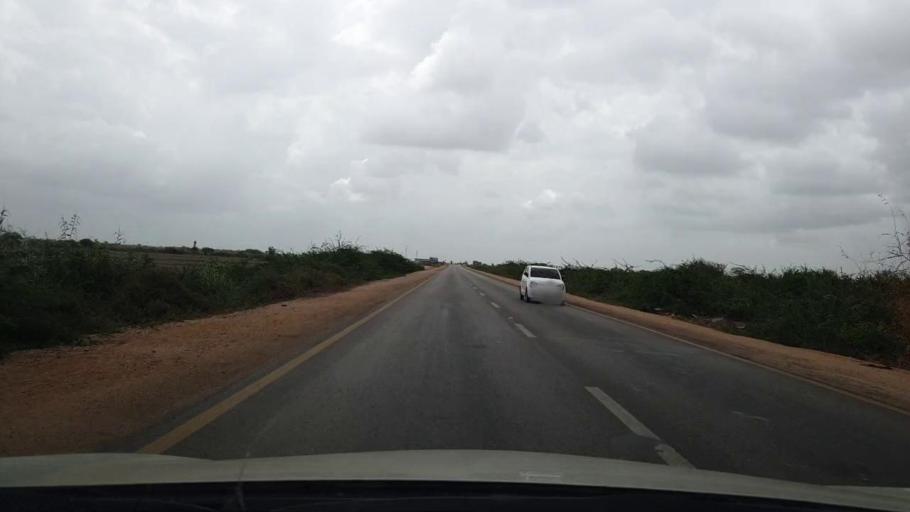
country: PK
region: Sindh
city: Mirpur Batoro
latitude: 24.6359
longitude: 68.3798
